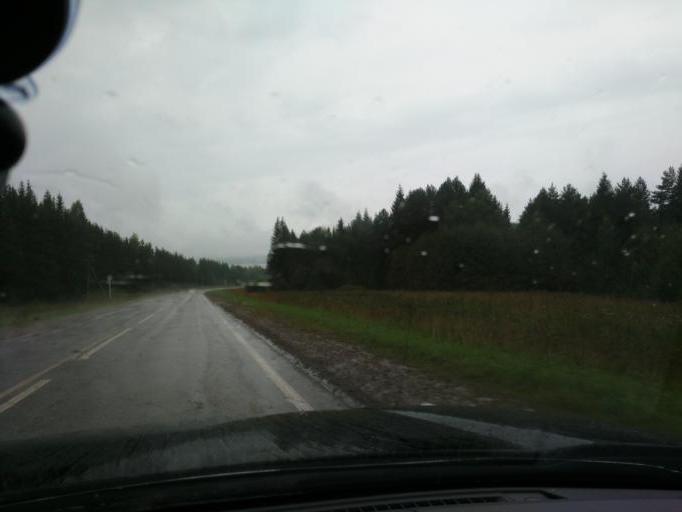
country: RU
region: Perm
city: Osa
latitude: 57.3254
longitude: 55.6044
